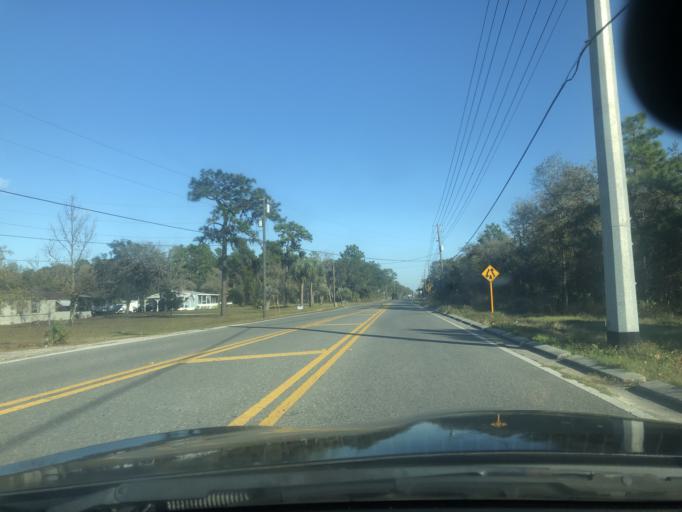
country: US
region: Florida
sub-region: Citrus County
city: Homosassa Springs
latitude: 28.7640
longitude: -82.5488
